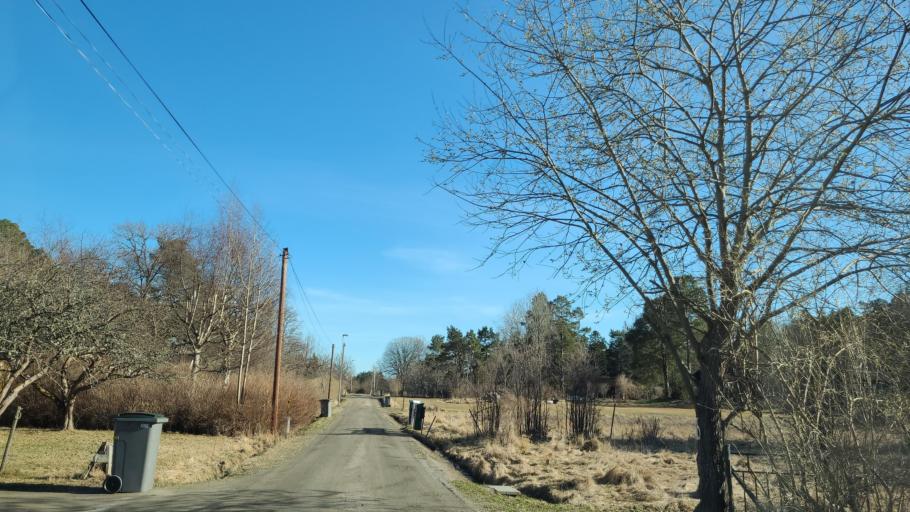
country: SE
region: Stockholm
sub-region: Varmdo Kommun
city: Holo
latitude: 59.3578
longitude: 18.6617
